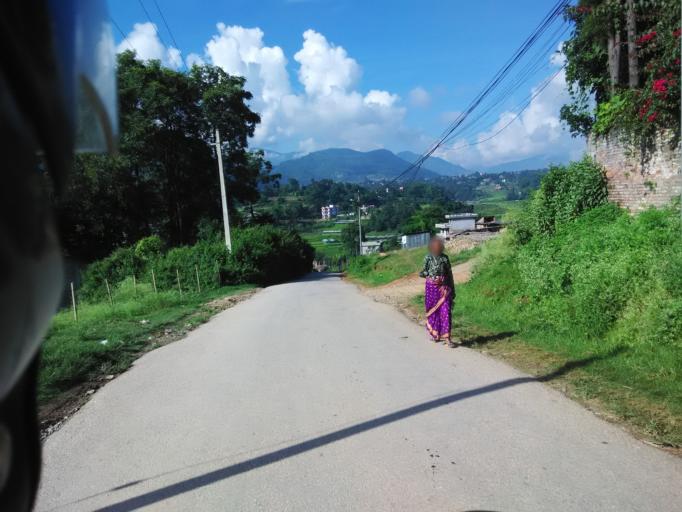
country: NP
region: Central Region
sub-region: Bagmati Zone
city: Patan
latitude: 27.6069
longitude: 85.3537
